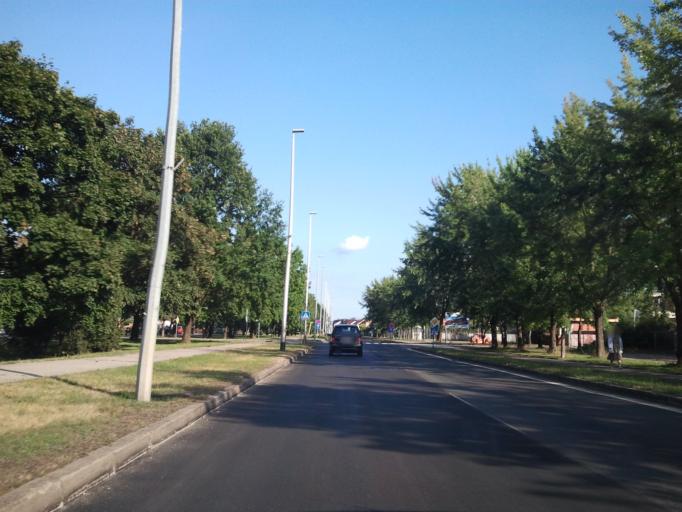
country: HR
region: Zagrebacka
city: Gradici
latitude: 45.7181
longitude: 16.0559
